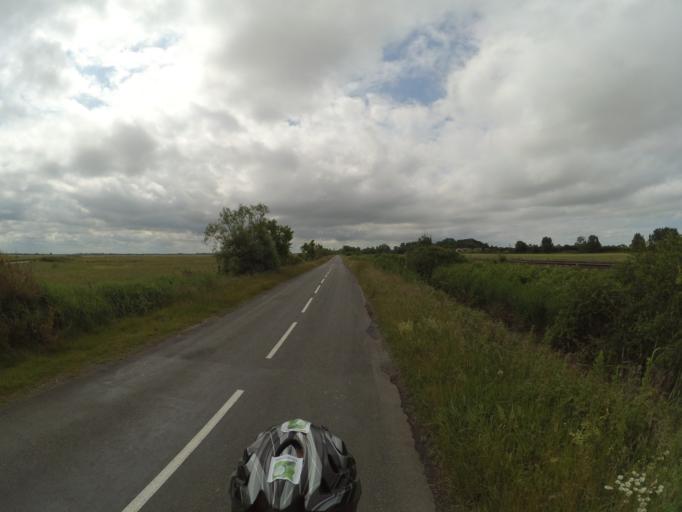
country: FR
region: Poitou-Charentes
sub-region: Departement de la Charente-Maritime
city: Yves
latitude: 46.0279
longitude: -1.0481
